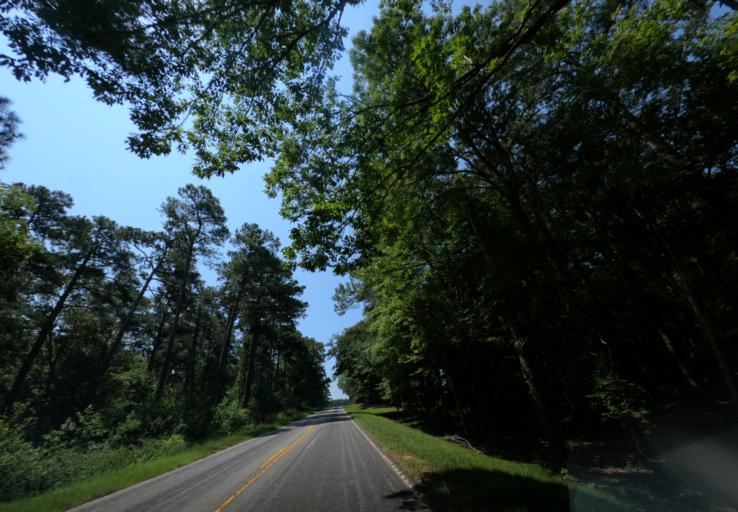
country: US
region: South Carolina
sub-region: McCormick County
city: McCormick
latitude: 33.9838
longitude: -82.1299
